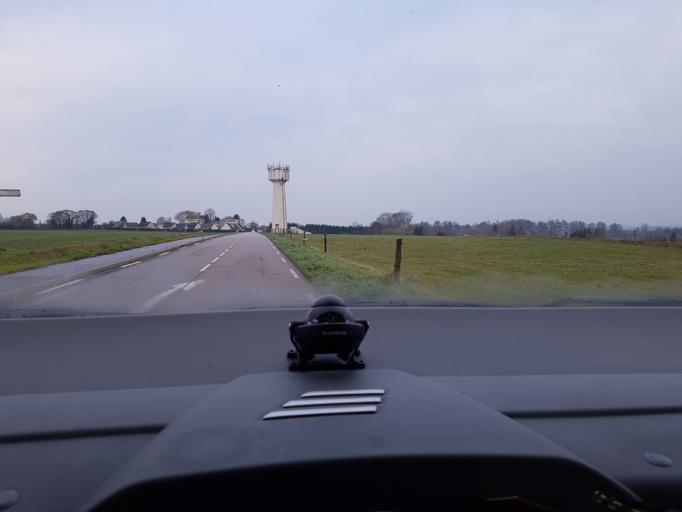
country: FR
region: Haute-Normandie
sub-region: Departement de la Seine-Maritime
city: Saint-Pierre-de-Varengeville
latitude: 49.5003
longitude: 0.9434
